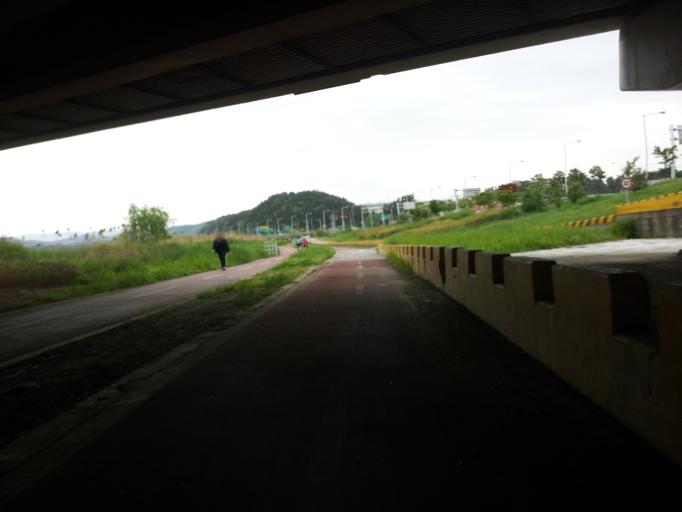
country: KR
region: Daejeon
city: Daejeon
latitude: 36.3569
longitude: 127.4045
